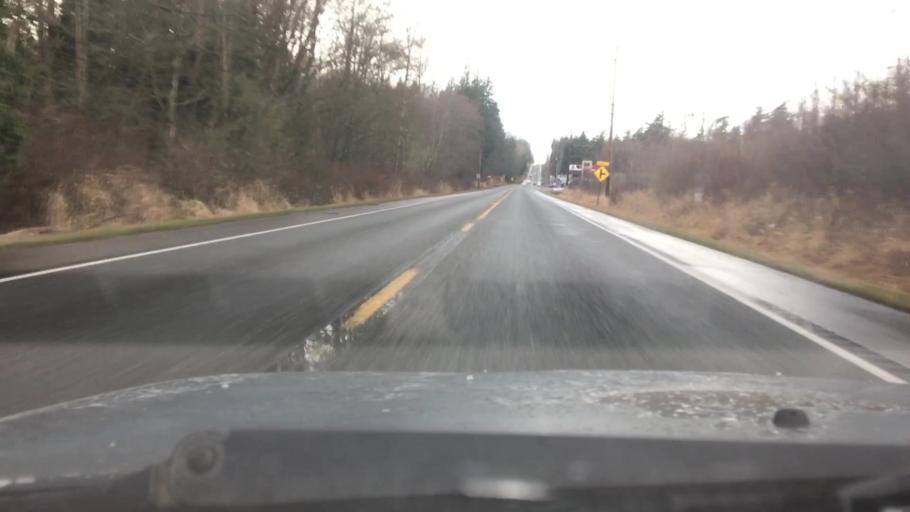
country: US
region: Washington
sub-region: Whatcom County
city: Ferndale
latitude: 48.8195
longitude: -122.6580
